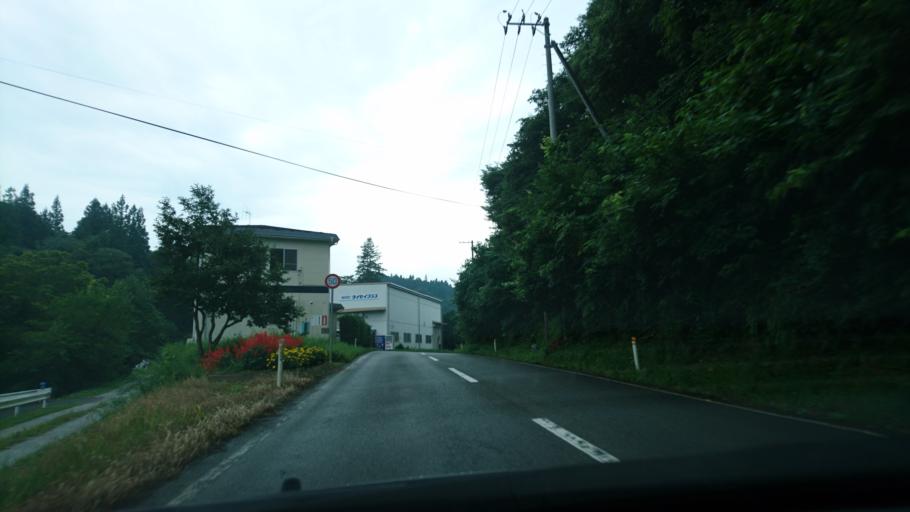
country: JP
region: Iwate
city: Ichinoseki
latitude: 39.0151
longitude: 141.2449
